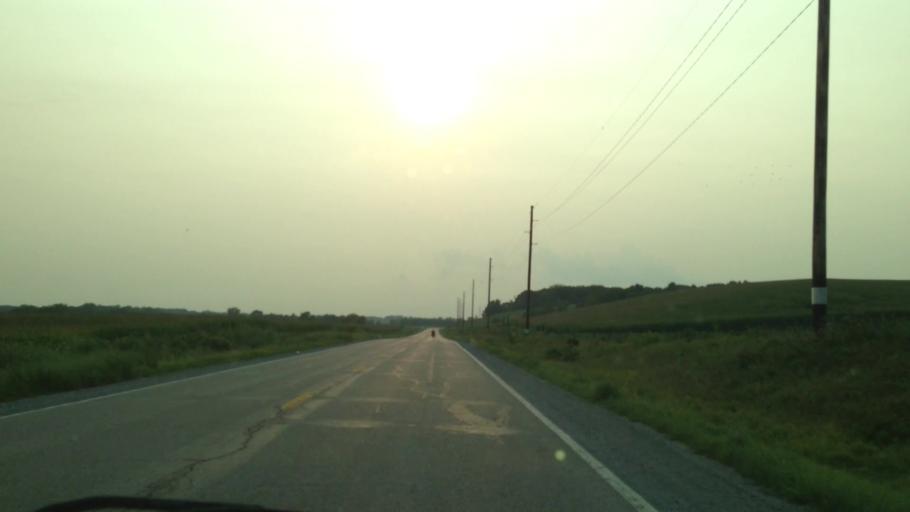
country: US
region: Iowa
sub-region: Benton County
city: Walford
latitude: 41.7976
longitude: -91.9190
